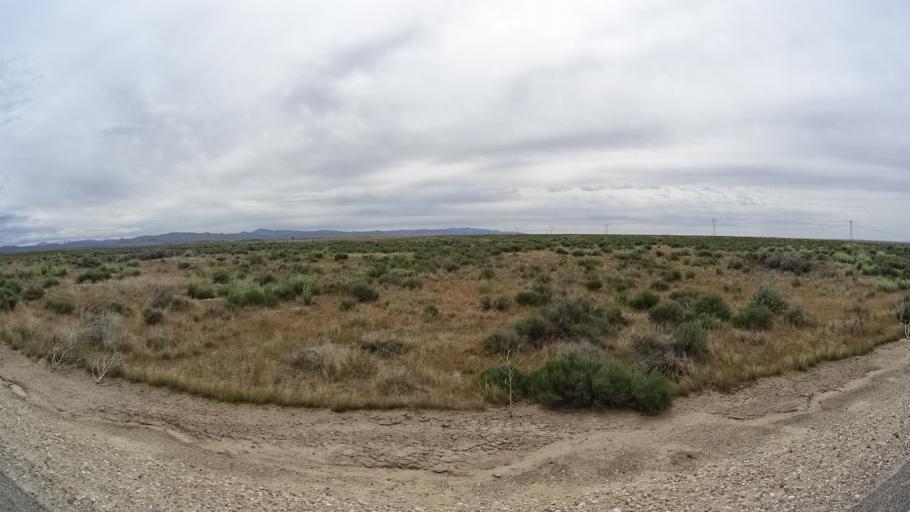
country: US
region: Idaho
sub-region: Ada County
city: Boise
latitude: 43.3790
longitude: -116.0045
